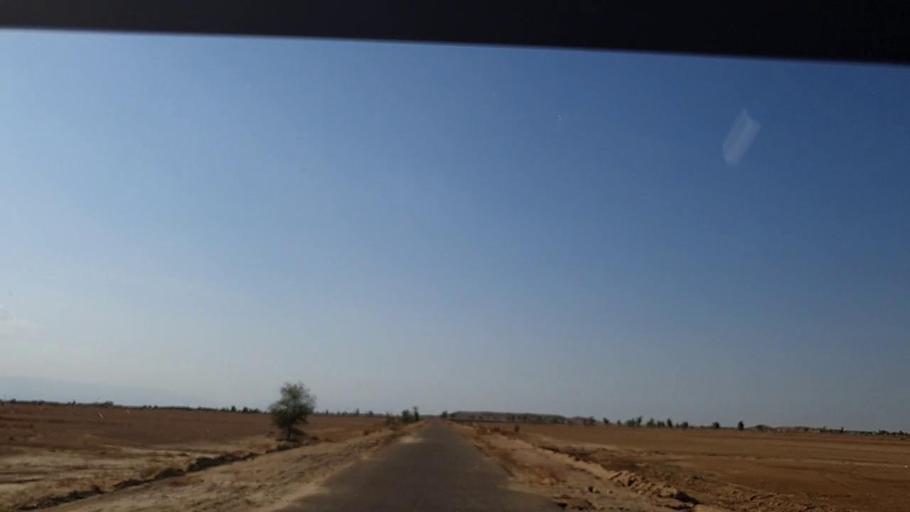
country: PK
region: Sindh
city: Johi
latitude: 26.5276
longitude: 67.5096
